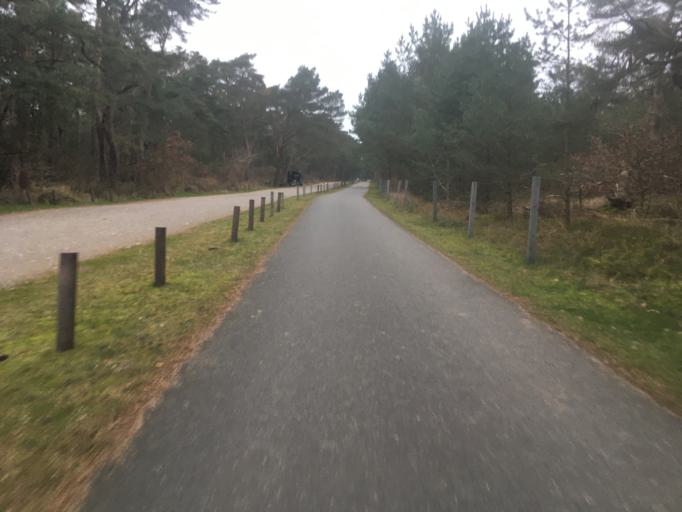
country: DE
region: Mecklenburg-Vorpommern
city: Sagard
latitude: 54.4662
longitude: 13.5664
